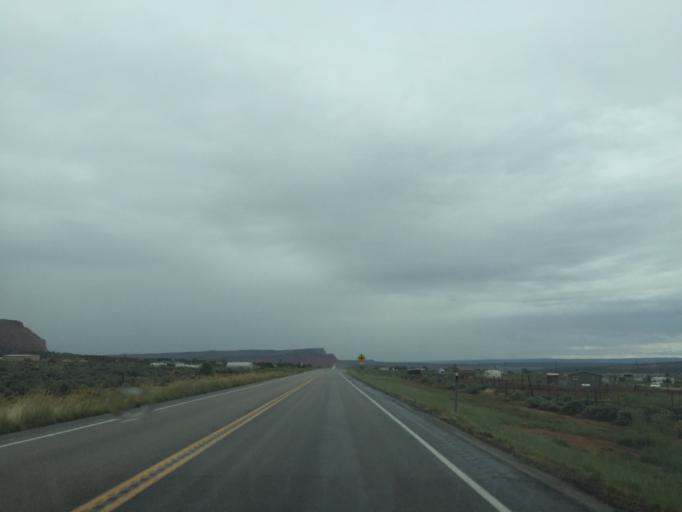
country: US
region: Utah
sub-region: Kane County
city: Kanab
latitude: 37.0261
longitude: -112.4204
